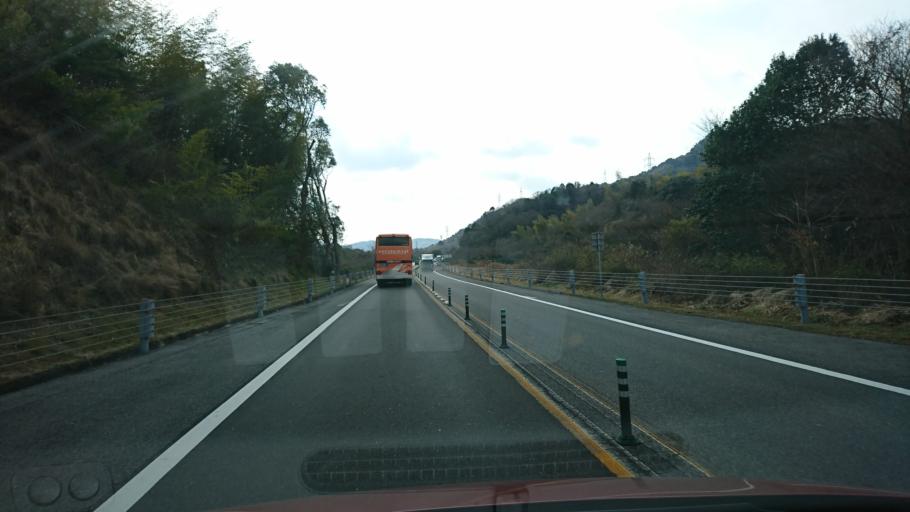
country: JP
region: Hiroshima
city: Innoshima
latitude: 34.2341
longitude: 133.0482
